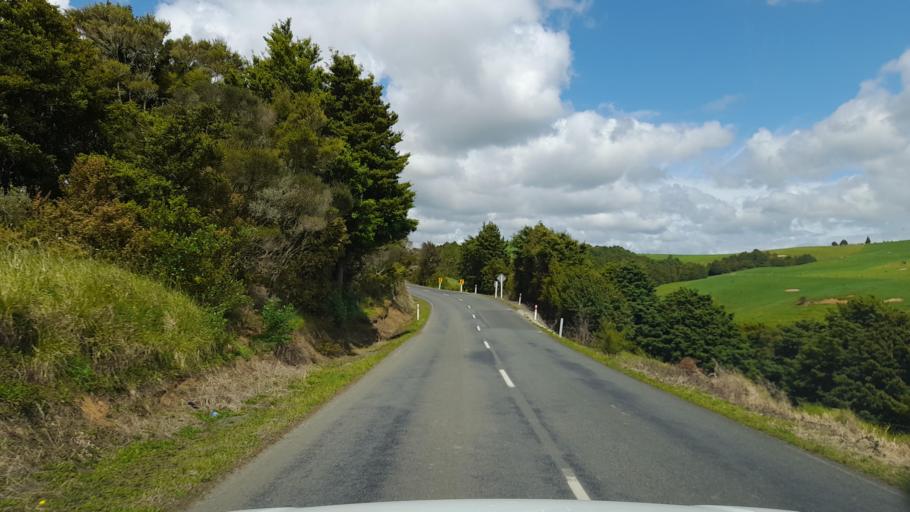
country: NZ
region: Northland
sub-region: Whangarei
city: Maungatapere
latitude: -35.6384
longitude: 174.0606
